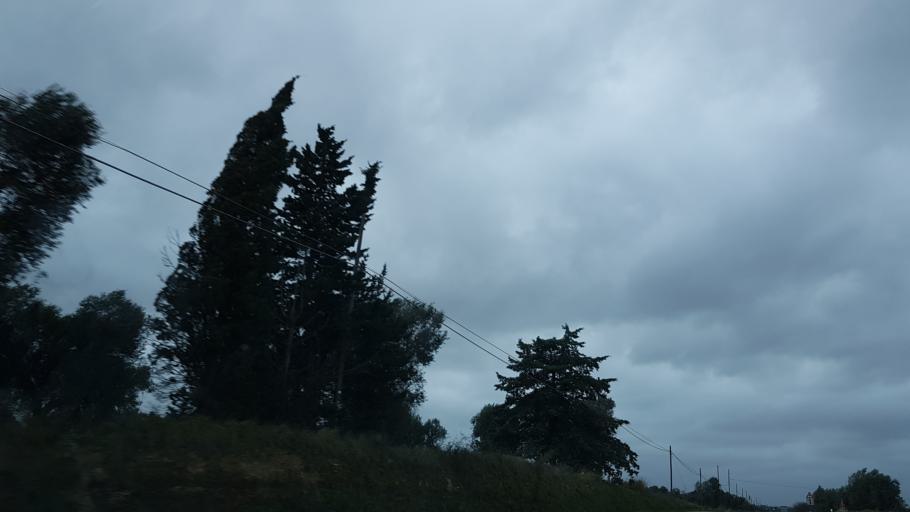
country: IT
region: Apulia
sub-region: Provincia di Brindisi
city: San Vito dei Normanni
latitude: 40.6524
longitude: 17.8006
